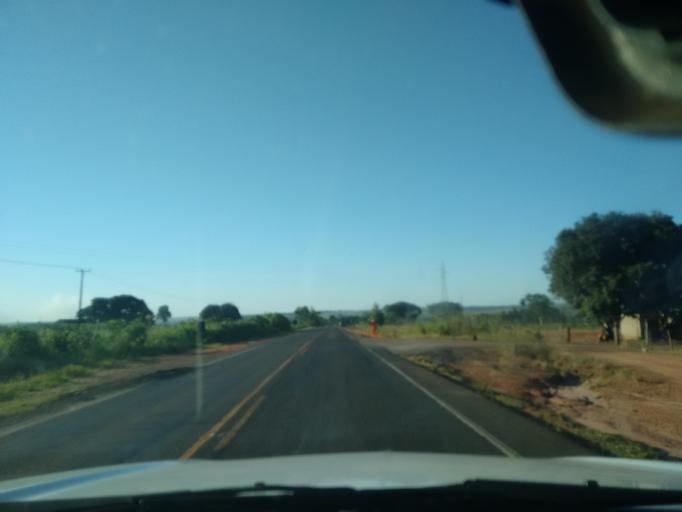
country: BR
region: Mato Grosso do Sul
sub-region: Eldorado
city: Eldorado
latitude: -23.8593
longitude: -54.3336
